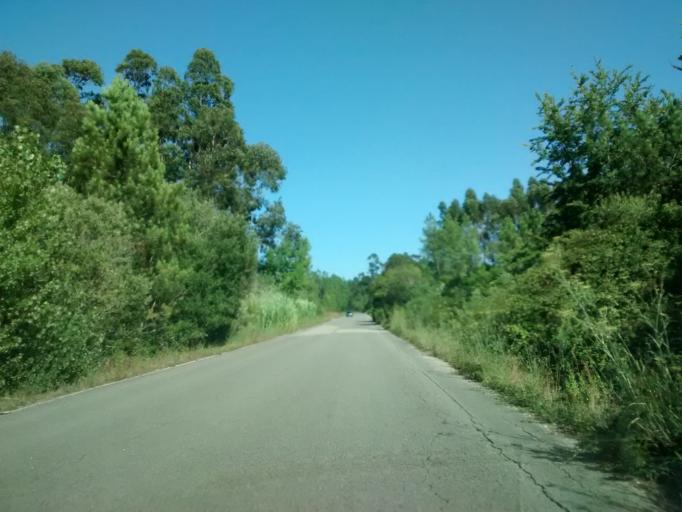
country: PT
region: Coimbra
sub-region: Cantanhede
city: Cantanhede
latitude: 40.4233
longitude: -8.6163
